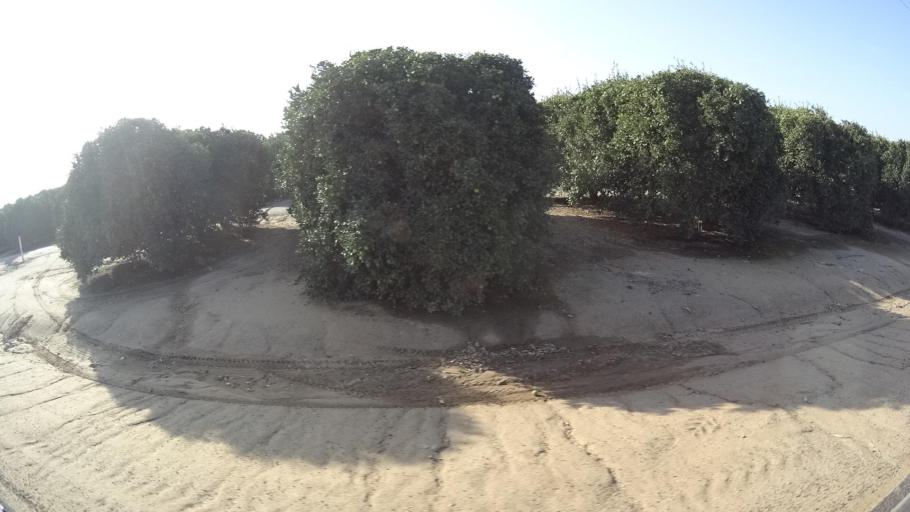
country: US
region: California
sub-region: Kern County
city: McFarland
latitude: 35.6676
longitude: -119.1171
